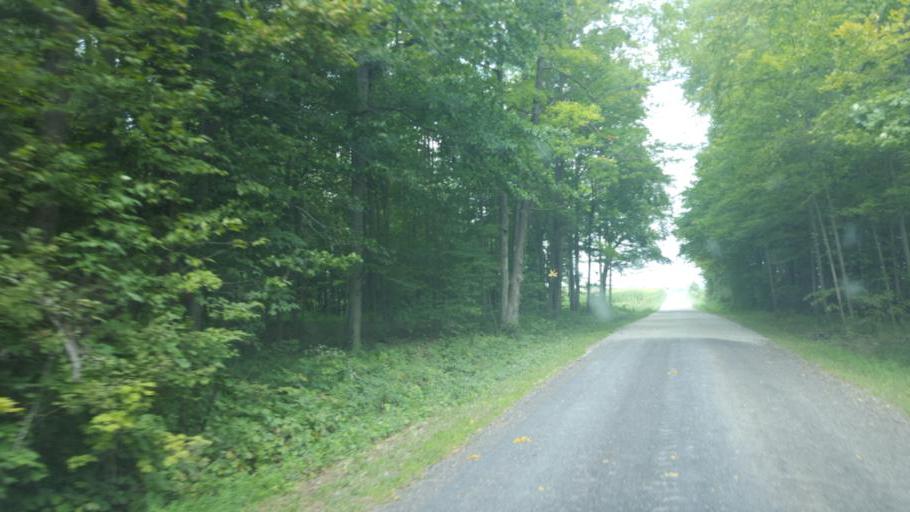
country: US
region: Ohio
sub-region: Morrow County
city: Mount Gilead
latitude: 40.6171
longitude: -82.7091
